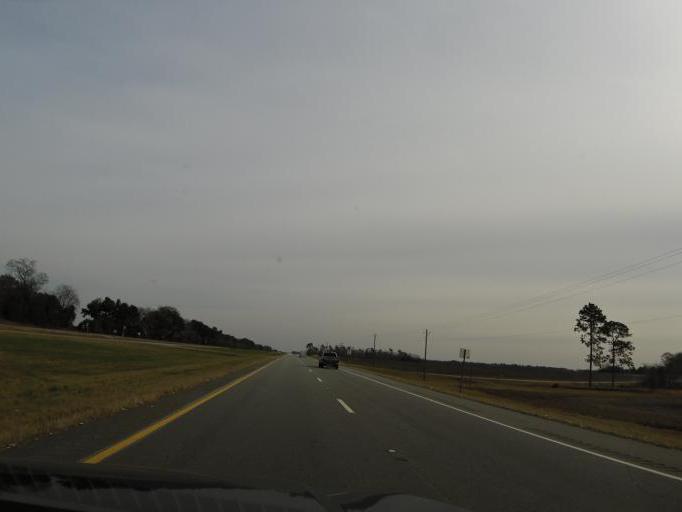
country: US
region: Georgia
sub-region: Seminole County
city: Donalsonville
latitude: 31.0772
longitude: -84.9640
